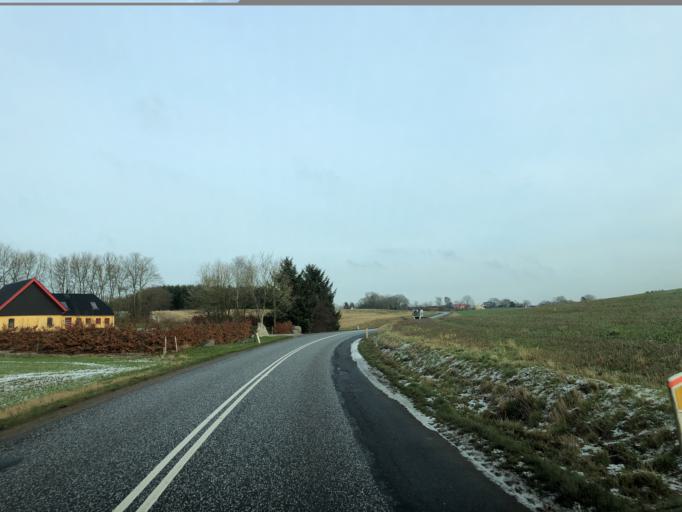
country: DK
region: Central Jutland
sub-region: Hedensted Kommune
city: Torring
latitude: 55.8088
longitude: 9.4644
